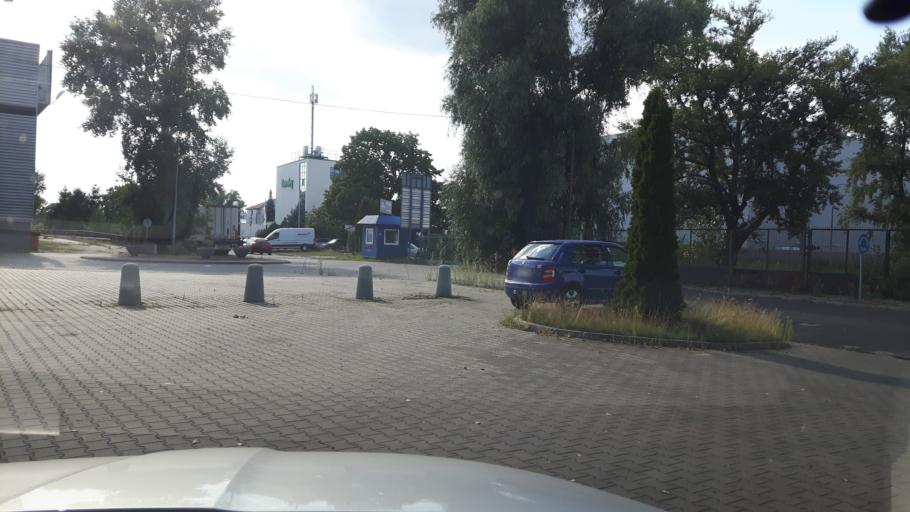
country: PL
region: Masovian Voivodeship
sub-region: Warszawa
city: Praga Polnoc
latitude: 52.2748
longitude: 21.0184
